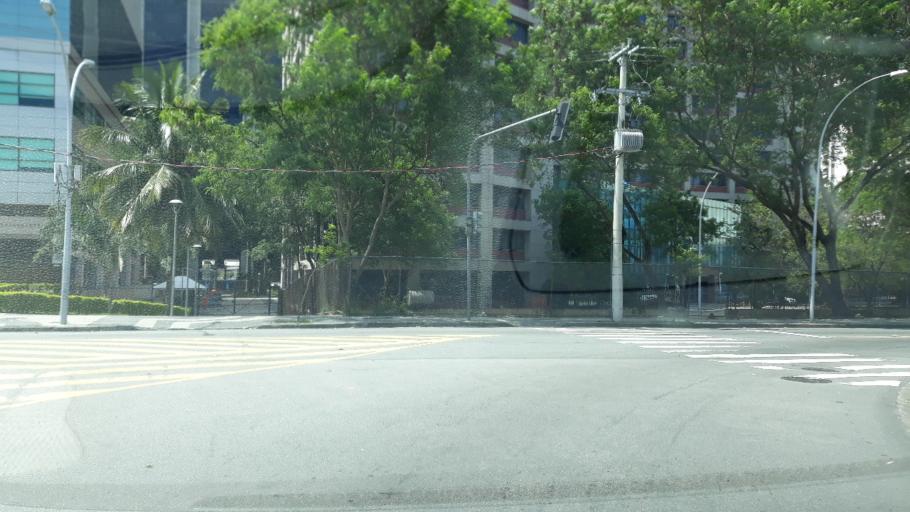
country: BR
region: Rio de Janeiro
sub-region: Rio De Janeiro
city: Rio de Janeiro
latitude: -22.9127
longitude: -43.2051
